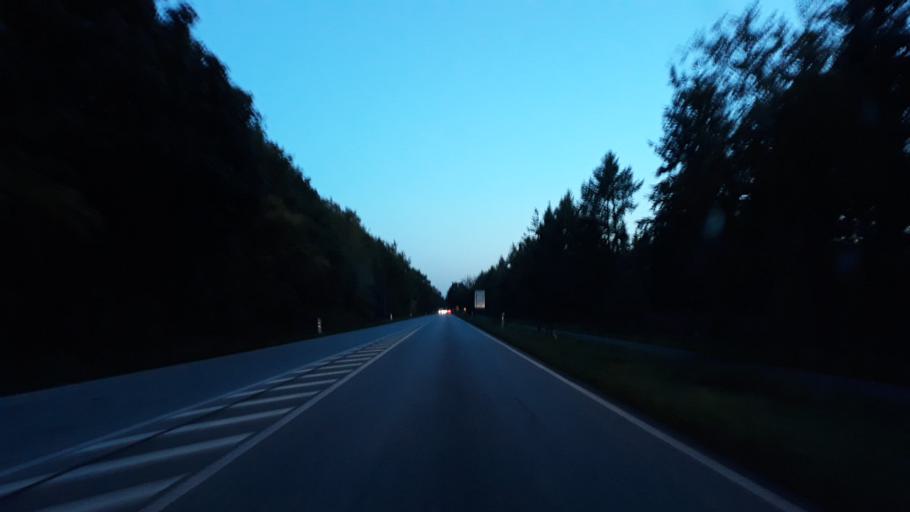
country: DE
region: Schleswig-Holstein
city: Kropp
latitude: 54.4117
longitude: 9.5312
